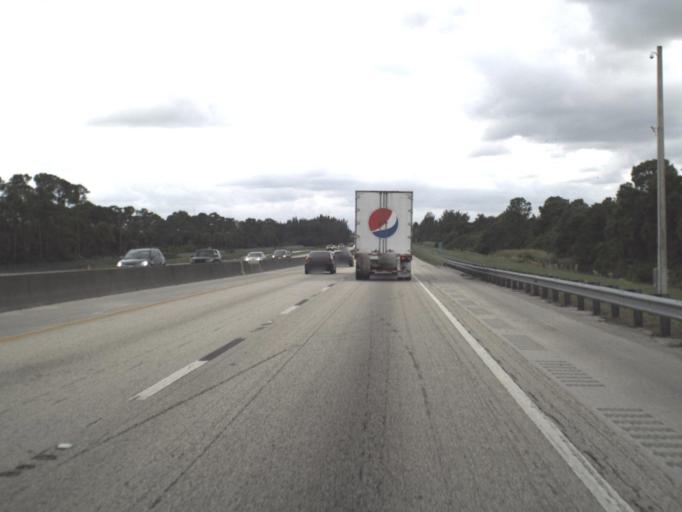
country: US
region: Florida
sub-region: Palm Beach County
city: Palm Beach Gardens
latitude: 26.7730
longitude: -80.1331
